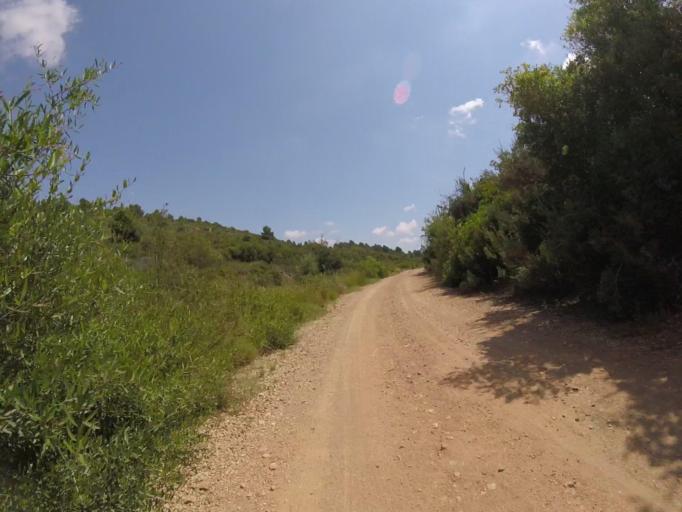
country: ES
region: Valencia
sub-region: Provincia de Castello
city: Torreblanca
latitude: 40.2129
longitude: 0.1393
